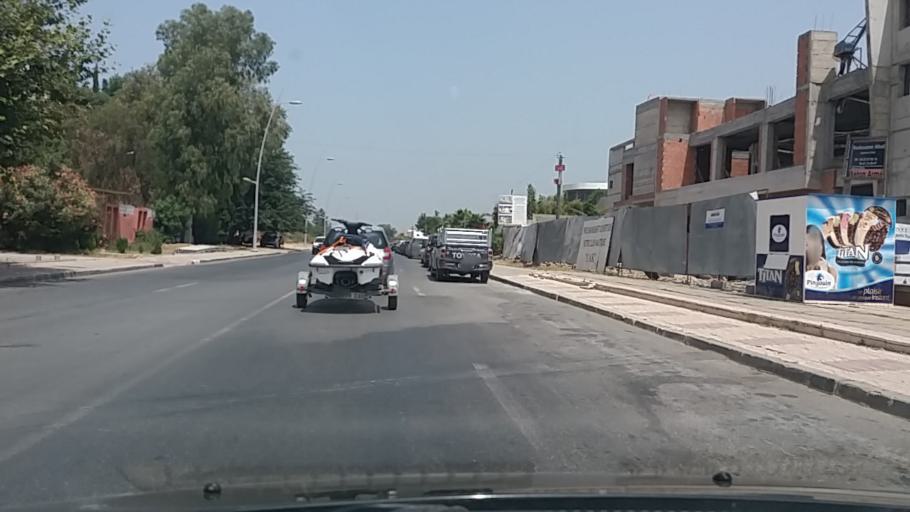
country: MA
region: Gharb-Chrarda-Beni Hssen
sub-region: Kenitra Province
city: Kenitra
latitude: 34.2694
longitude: -6.5915
